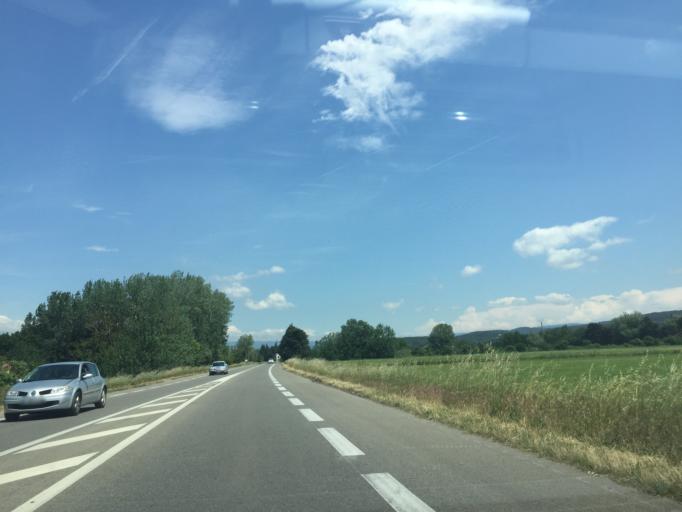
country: FR
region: Provence-Alpes-Cote d'Azur
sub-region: Departement du Vaucluse
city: Velleron
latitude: 43.9826
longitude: 5.0195
